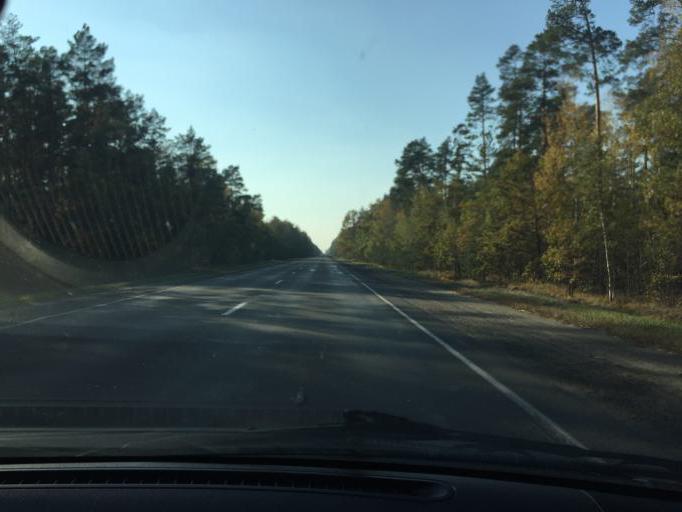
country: BY
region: Brest
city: Mikashevichy
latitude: 52.2464
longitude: 27.3798
